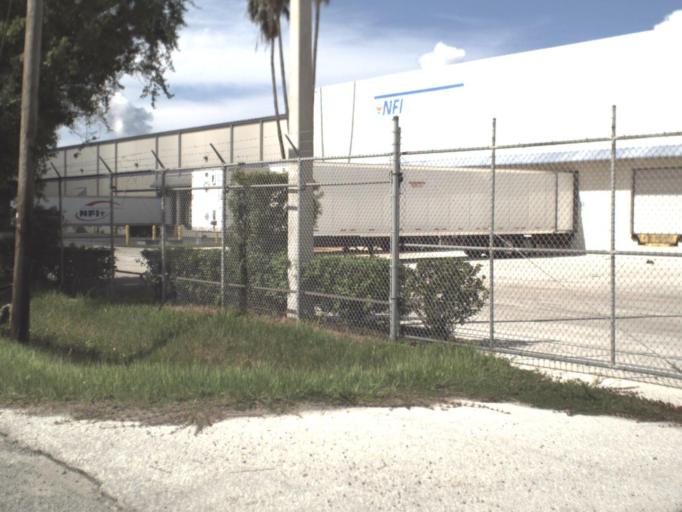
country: US
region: Florida
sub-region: Hillsborough County
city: East Lake-Orient Park
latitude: 27.9624
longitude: -82.3853
